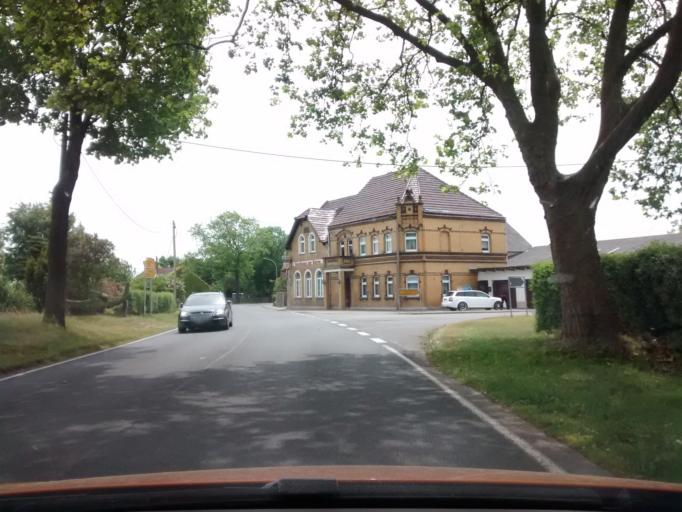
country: DE
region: Brandenburg
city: Juterbog
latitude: 51.9317
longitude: 13.1223
